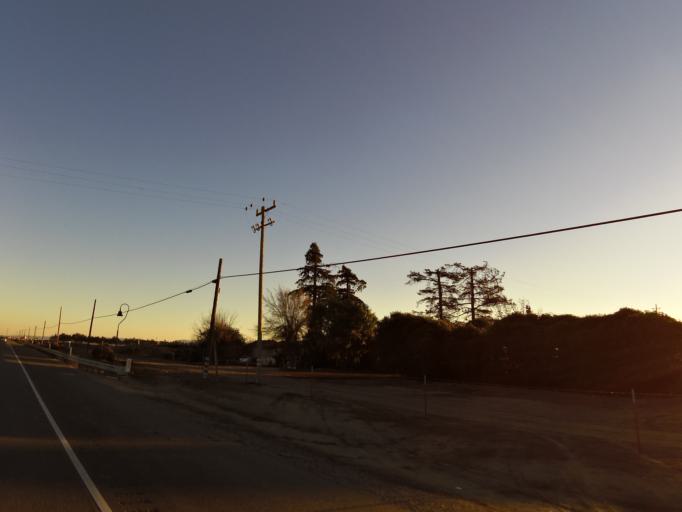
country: US
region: California
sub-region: Monterey County
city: Greenfield
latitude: 36.2855
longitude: -121.1930
